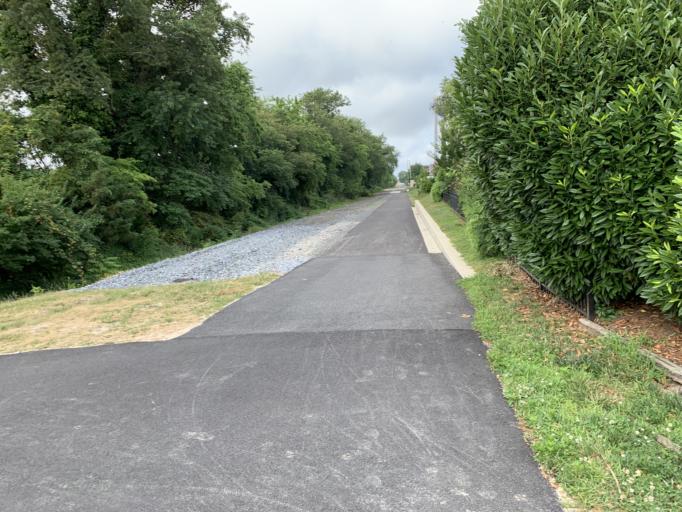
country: US
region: Delaware
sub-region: Sussex County
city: Lewes
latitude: 38.7733
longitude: -75.1344
